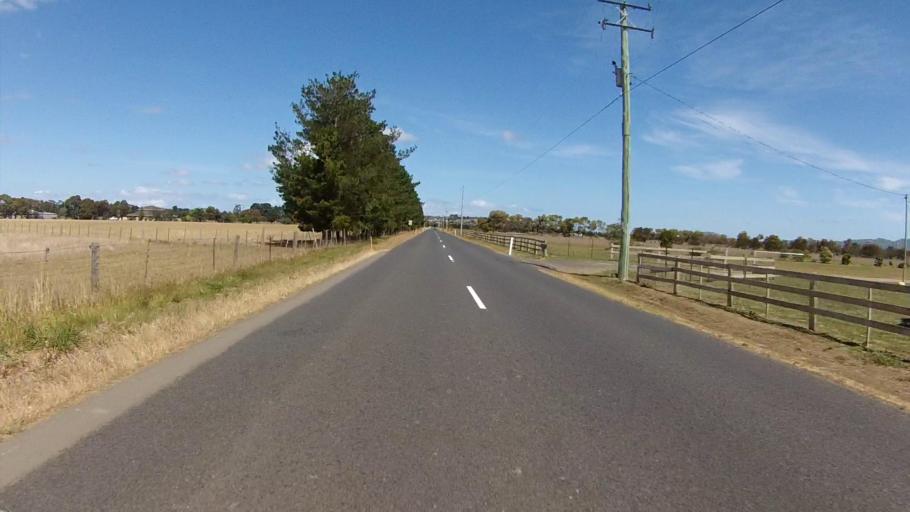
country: AU
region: Tasmania
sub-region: Sorell
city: Sorell
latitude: -42.7706
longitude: 147.5174
